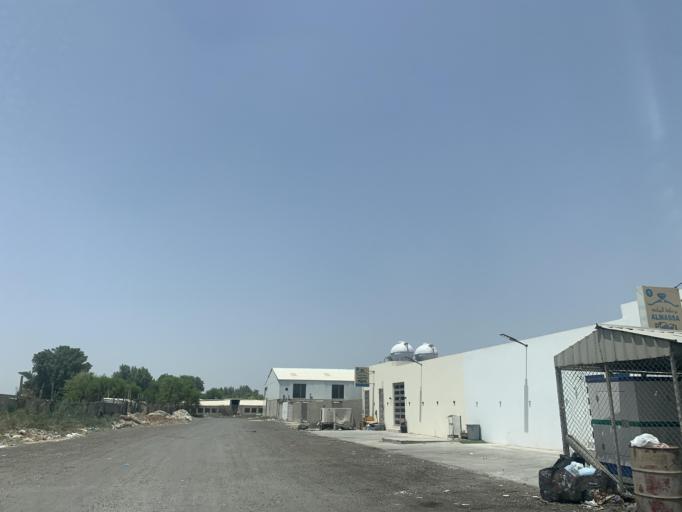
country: BH
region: Central Governorate
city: Madinat Hamad
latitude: 26.1541
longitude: 50.4941
